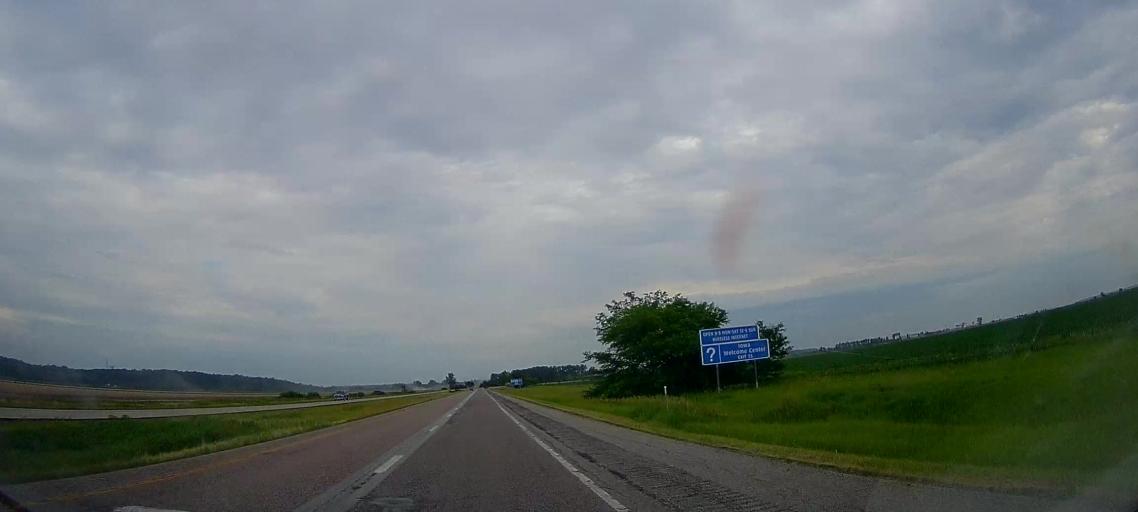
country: US
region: Iowa
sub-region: Harrison County
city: Missouri Valley
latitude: 41.5717
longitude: -95.9250
